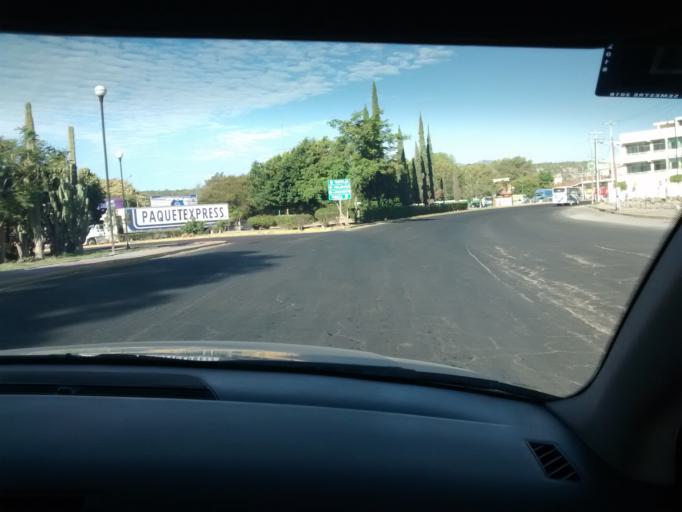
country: MX
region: Puebla
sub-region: Santiago Miahuatlan
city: San Jose Monte Chiquito
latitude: 18.4744
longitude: -97.4283
